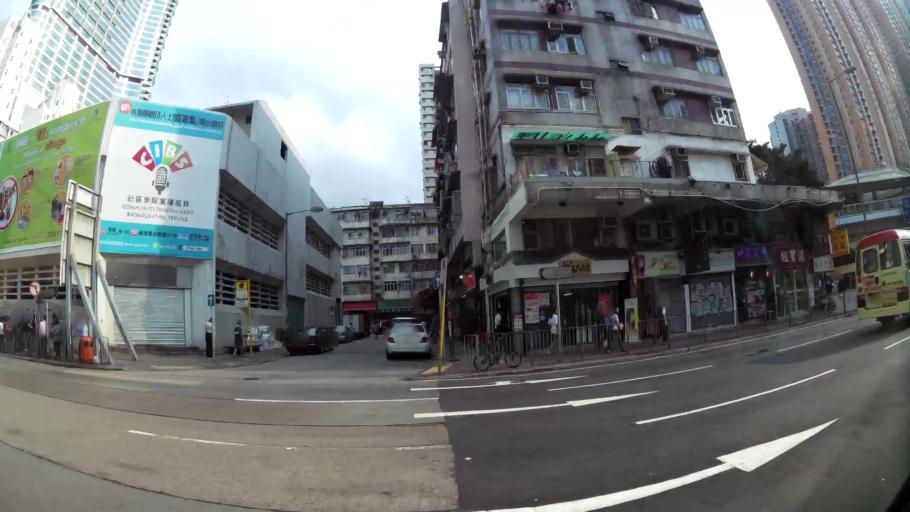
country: HK
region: Sham Shui Po
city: Sham Shui Po
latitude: 22.3188
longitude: 114.1667
